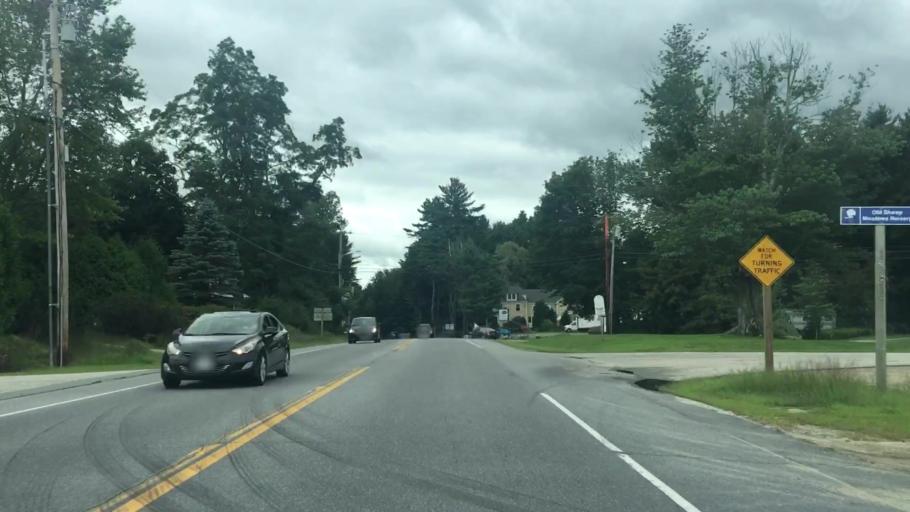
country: US
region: Maine
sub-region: York County
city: Alfred
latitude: 43.4884
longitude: -70.7197
